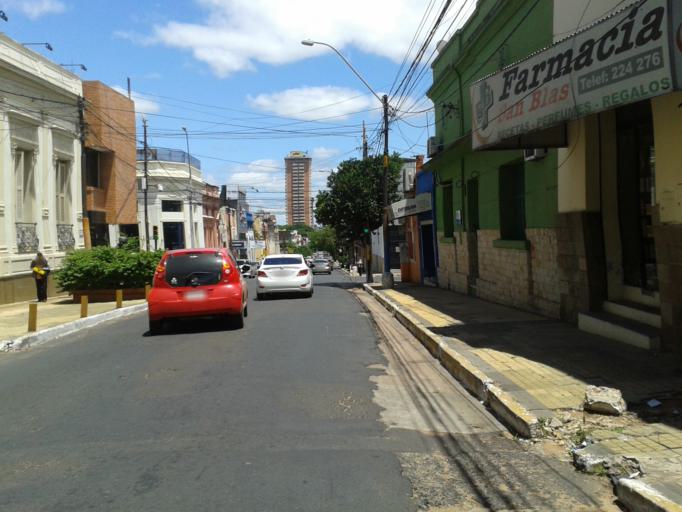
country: PY
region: Asuncion
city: Asuncion
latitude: -25.2866
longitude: -57.6253
